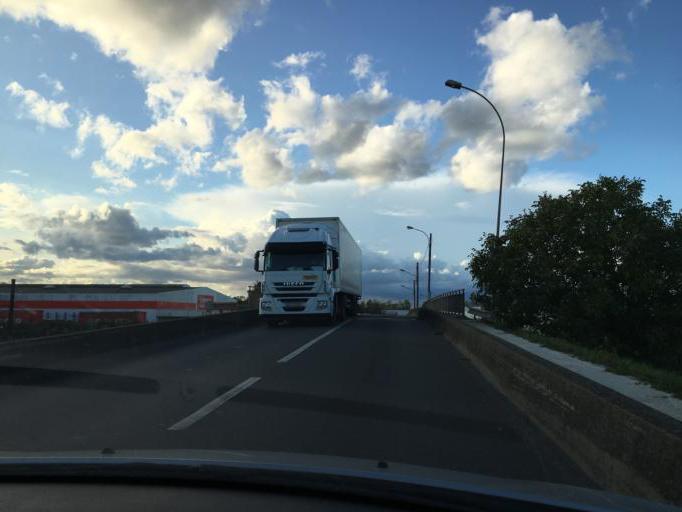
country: FR
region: Centre
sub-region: Departement du Loiret
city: Saint-Jean-de-la-Ruelle
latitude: 47.9009
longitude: 1.8506
